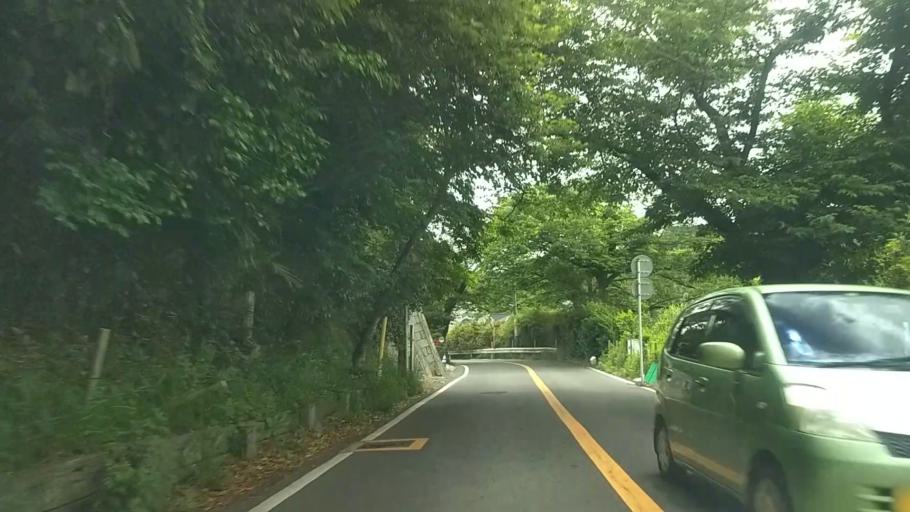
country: JP
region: Kanagawa
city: Kamakura
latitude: 35.3196
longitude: 139.5211
